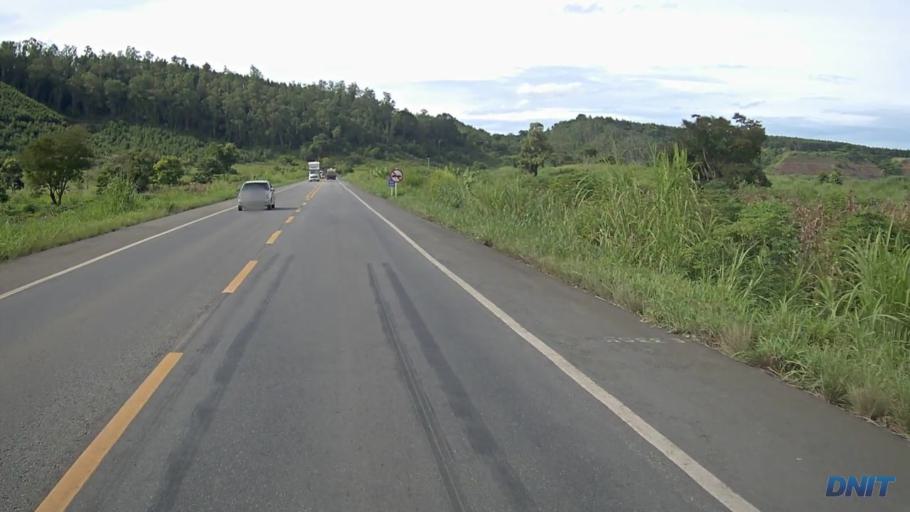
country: BR
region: Minas Gerais
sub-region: Belo Oriente
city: Belo Oriente
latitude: -19.2740
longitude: -42.3567
